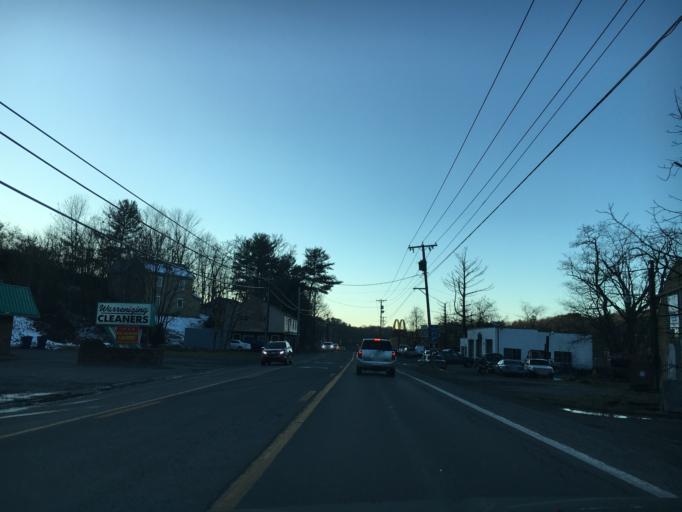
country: US
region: West Virginia
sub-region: Raleigh County
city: Daniels
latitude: 37.7486
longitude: -81.1318
